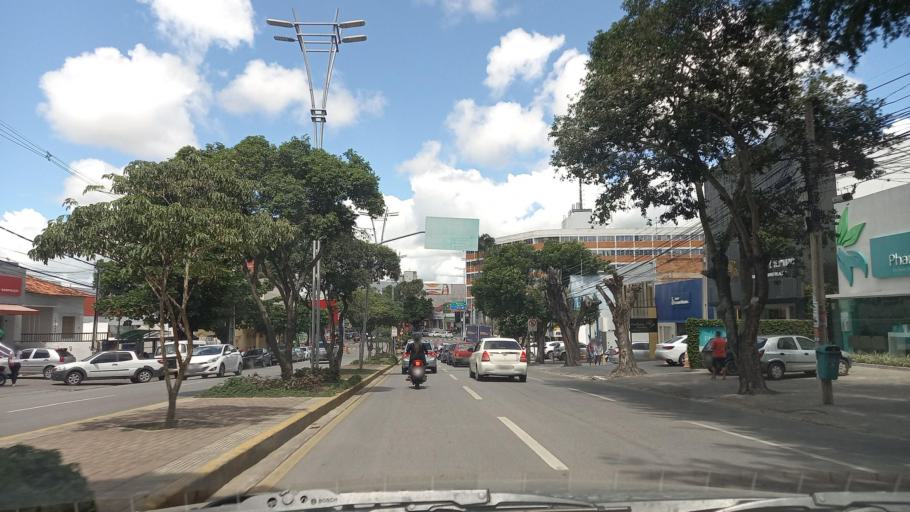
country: BR
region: Pernambuco
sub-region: Caruaru
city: Caruaru
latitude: -8.2814
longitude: -35.9715
